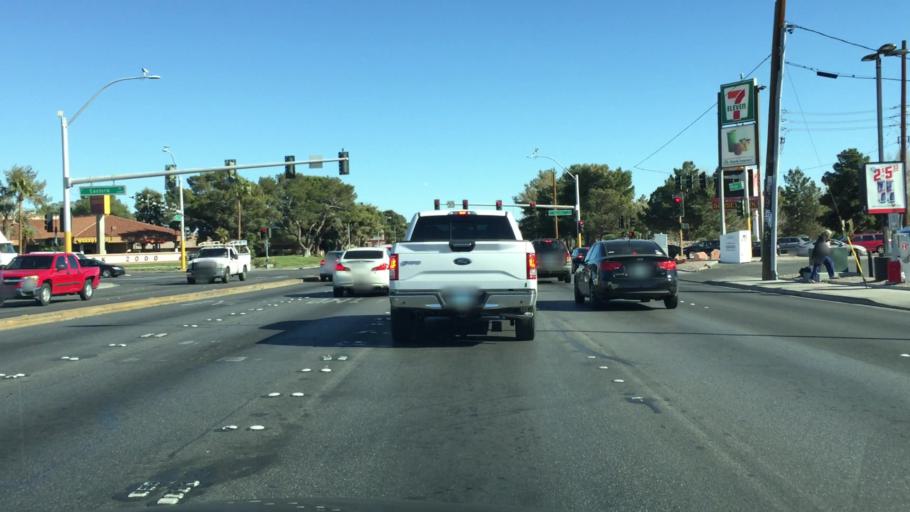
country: US
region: Nevada
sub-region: Clark County
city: Whitney
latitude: 36.0716
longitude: -115.1195
